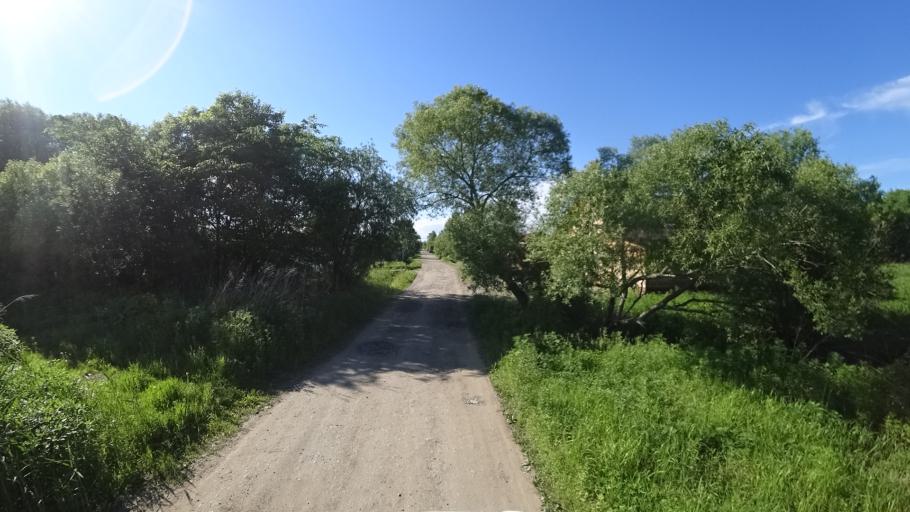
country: RU
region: Khabarovsk Krai
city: Khor
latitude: 47.8923
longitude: 134.9953
